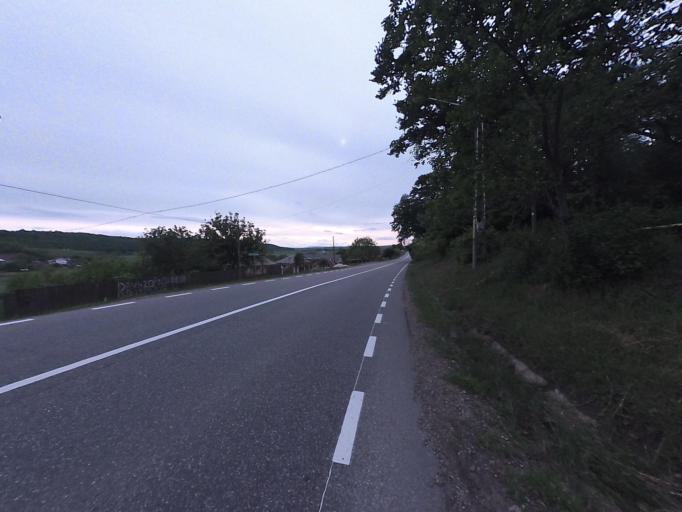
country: RO
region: Neamt
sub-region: Comuna Dulcesti
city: Dulcesti
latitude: 46.9663
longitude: 26.7844
